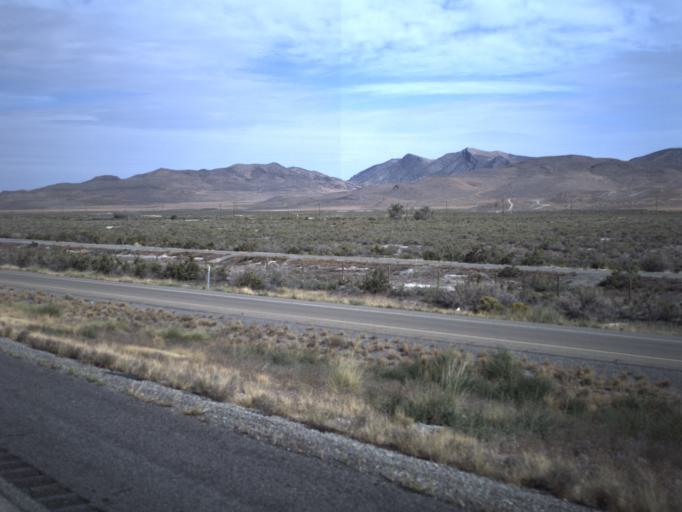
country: US
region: Utah
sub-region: Tooele County
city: Grantsville
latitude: 40.7640
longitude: -112.7833
